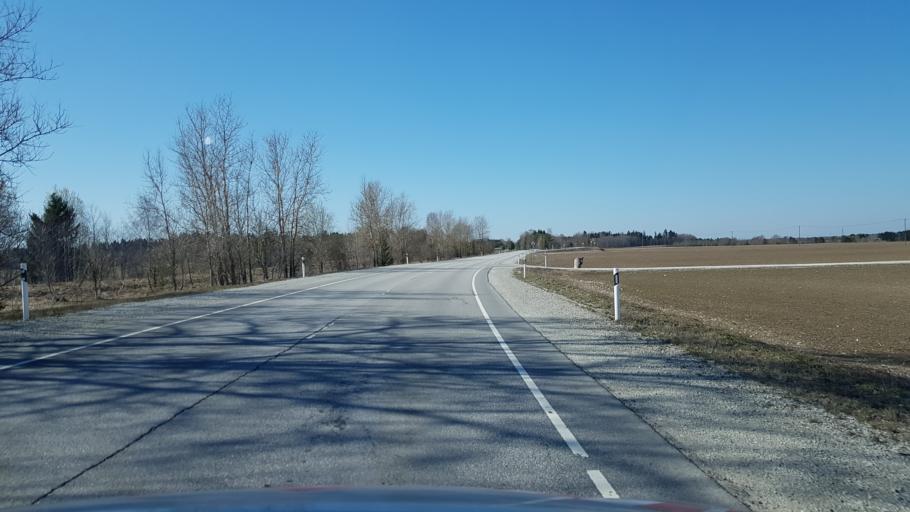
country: EE
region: Ida-Virumaa
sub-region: Kohtla-Nomme vald
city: Kohtla-Nomme
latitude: 59.3166
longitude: 27.2492
